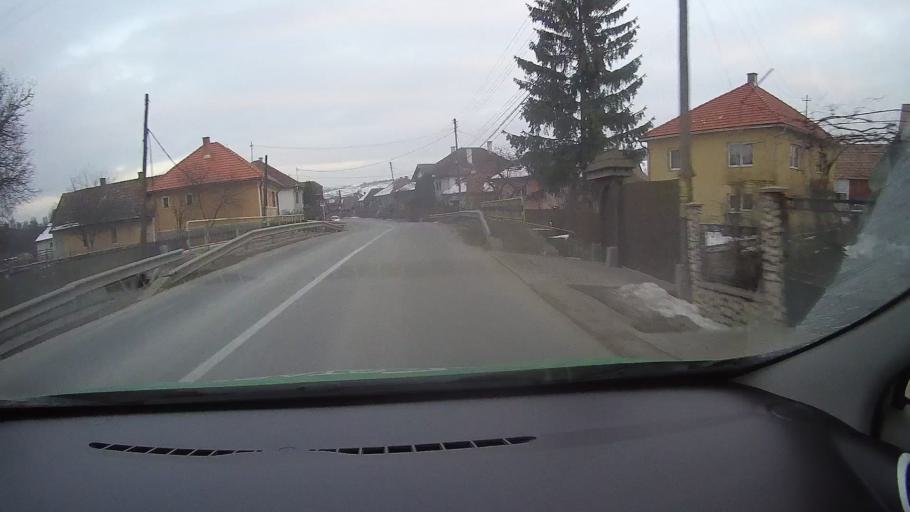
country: RO
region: Harghita
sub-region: Comuna Lupeni
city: Lupeni
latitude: 46.3567
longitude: 25.2232
